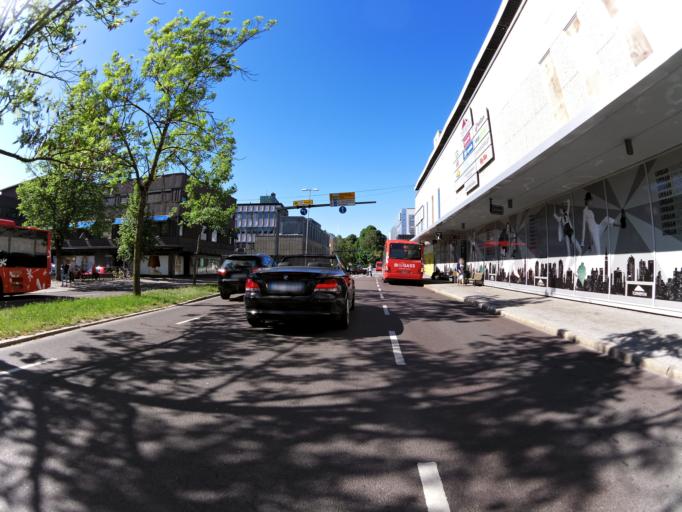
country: NO
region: Ostfold
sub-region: Fredrikstad
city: Fredrikstad
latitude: 59.2137
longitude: 10.9390
